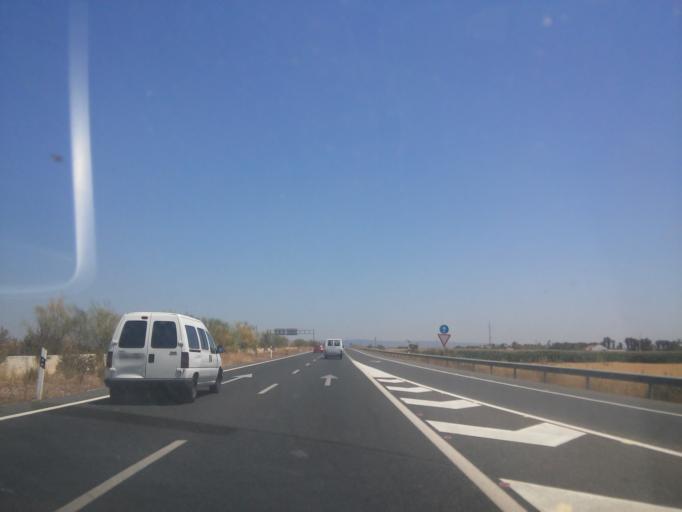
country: ES
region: Andalusia
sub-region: Provincia de Sevilla
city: La Rinconada
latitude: 37.4554
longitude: -5.9698
